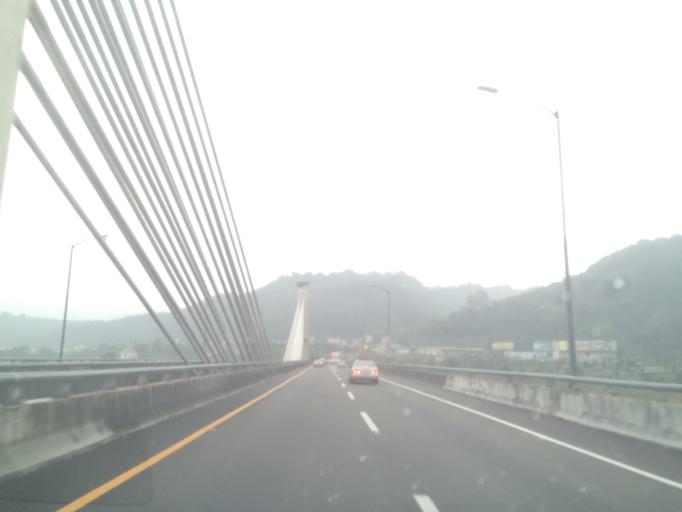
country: TW
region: Taiwan
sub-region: Nantou
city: Puli
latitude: 23.9776
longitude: 120.9268
